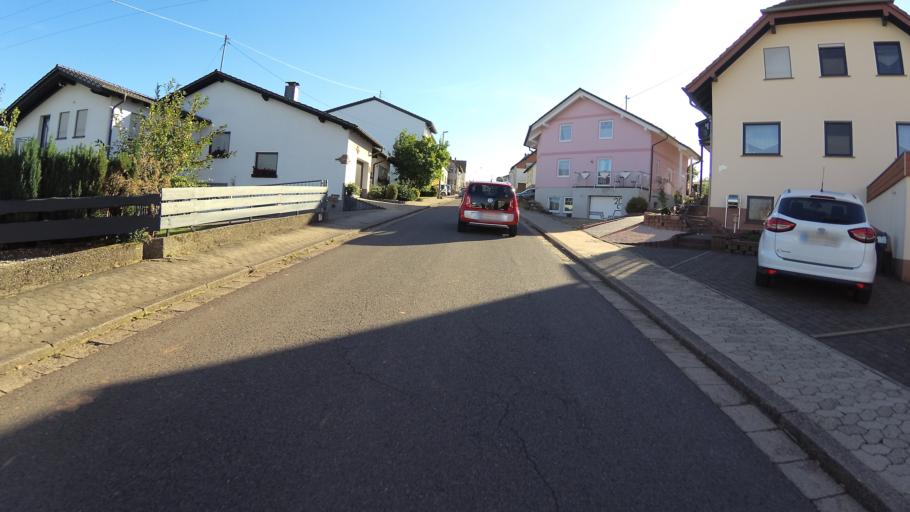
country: DE
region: Saarland
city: Eppelborn
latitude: 49.4028
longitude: 6.9556
